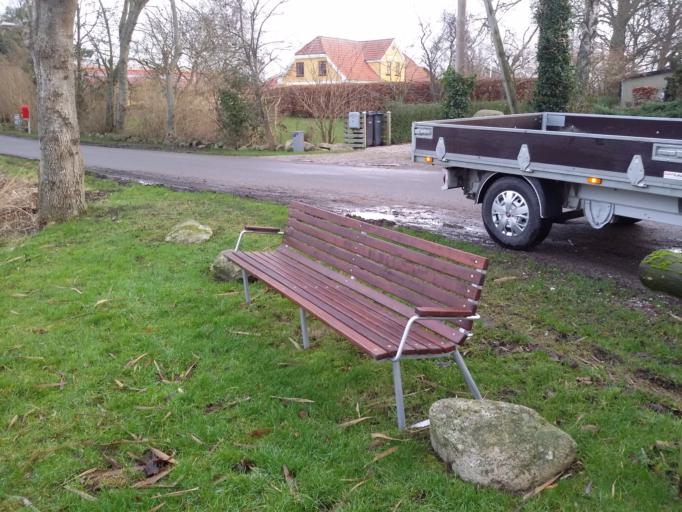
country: DK
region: Zealand
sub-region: Roskilde Kommune
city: Jyllinge
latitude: 55.7901
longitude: 12.1056
